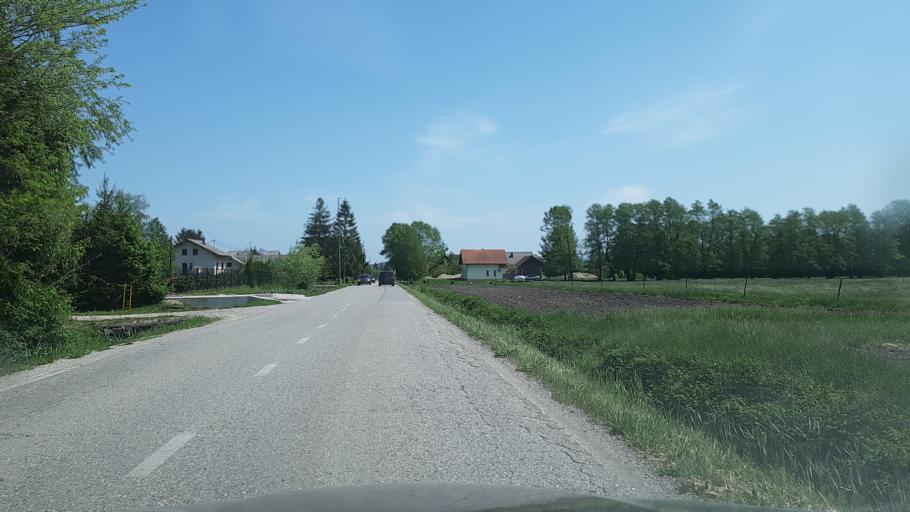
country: SI
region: Brezovica
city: Vnanje Gorice
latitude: 45.9990
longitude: 14.4736
